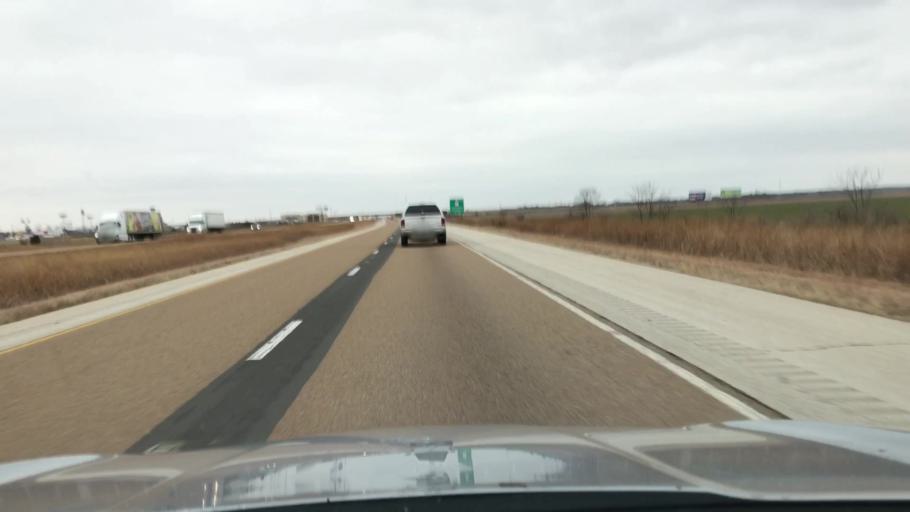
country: US
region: Illinois
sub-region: Montgomery County
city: Litchfield
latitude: 39.1871
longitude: -89.6735
